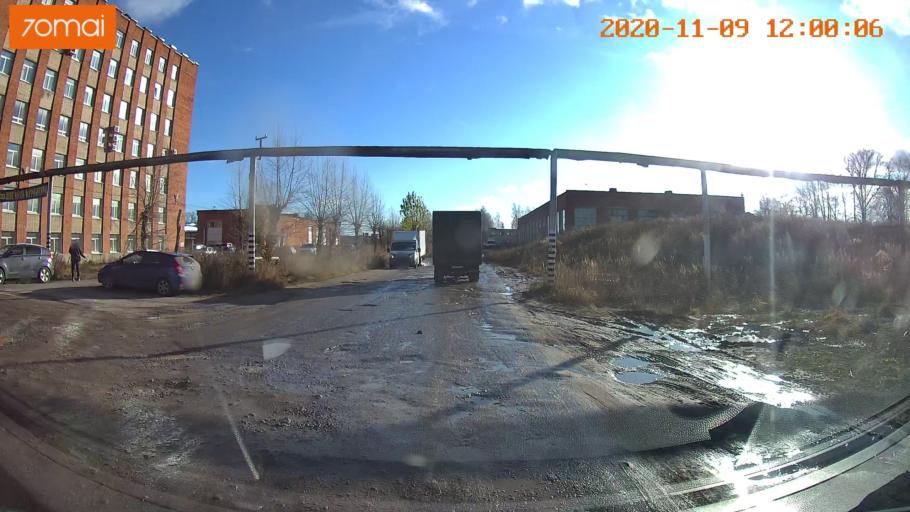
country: RU
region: Ivanovo
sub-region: Gorod Ivanovo
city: Ivanovo
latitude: 56.9843
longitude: 41.0197
